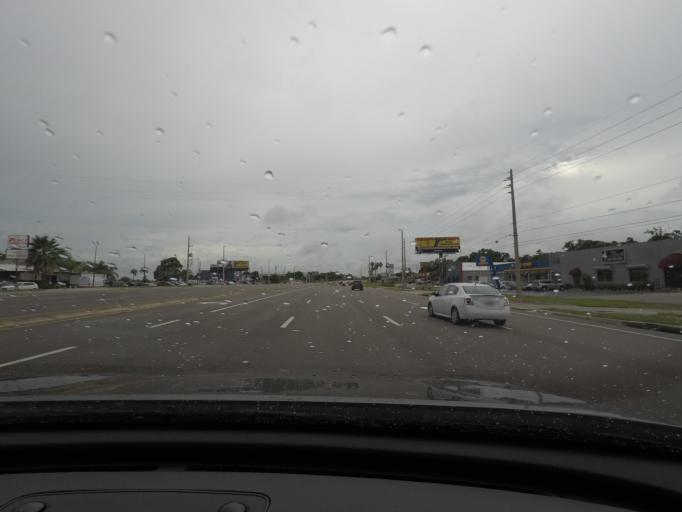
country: US
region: Florida
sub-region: Orange County
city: Azalea Park
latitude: 28.5546
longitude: -81.3168
